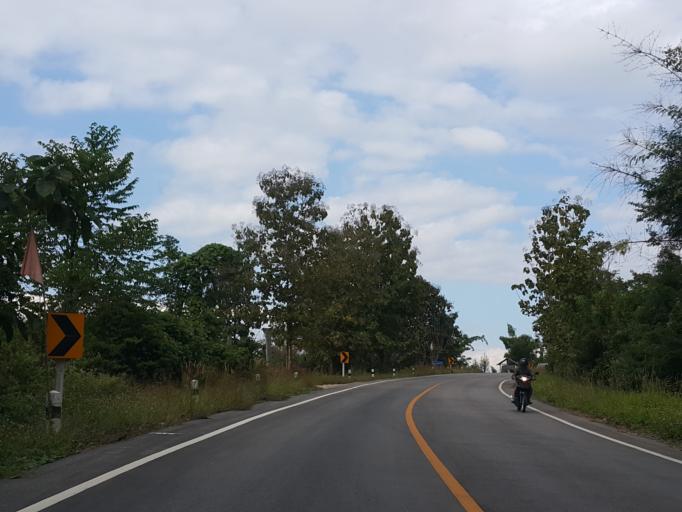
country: TH
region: Lampang
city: Chae Hom
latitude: 18.6167
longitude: 99.4813
